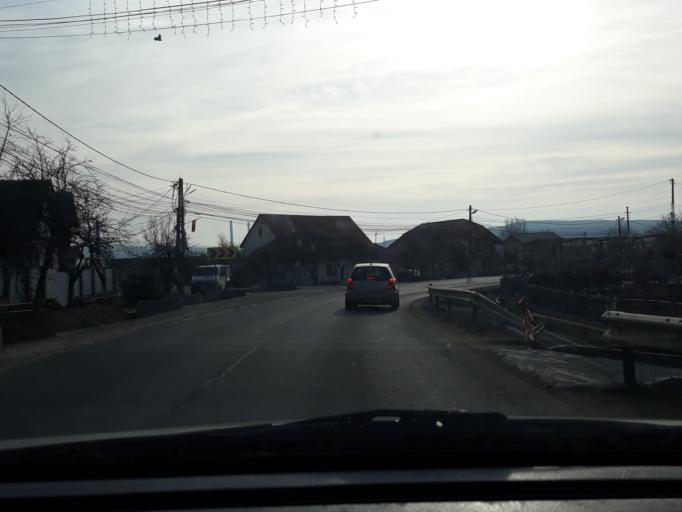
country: RO
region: Salaj
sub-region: Comuna Criseni
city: Criseni
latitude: 47.2308
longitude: 23.0445
